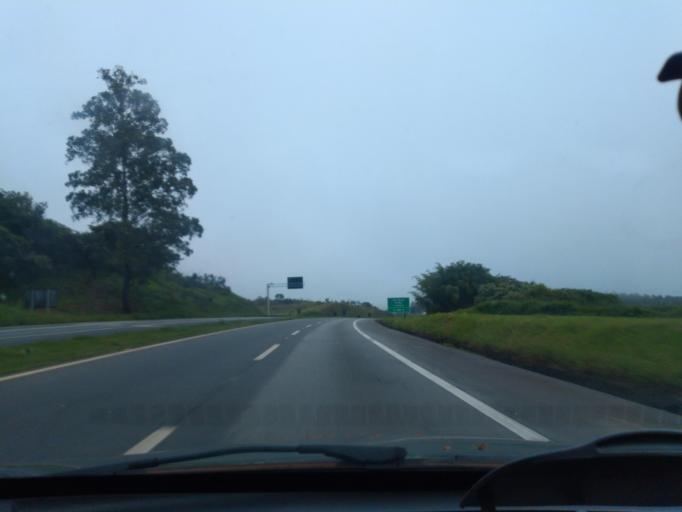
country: BR
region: Minas Gerais
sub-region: Tres Coracoes
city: Tres Coracoes
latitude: -21.4759
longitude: -45.2028
